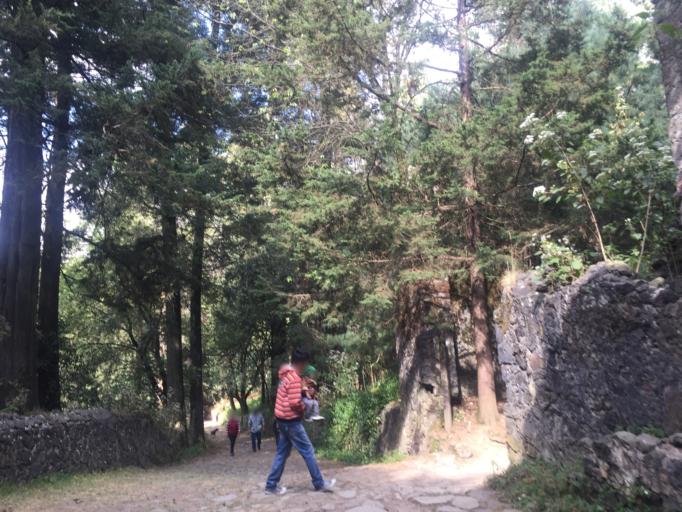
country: MX
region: Mexico City
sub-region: Cuajimalpa de Morelos
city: San Lorenzo Acopilco
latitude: 19.3154
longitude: -99.3098
